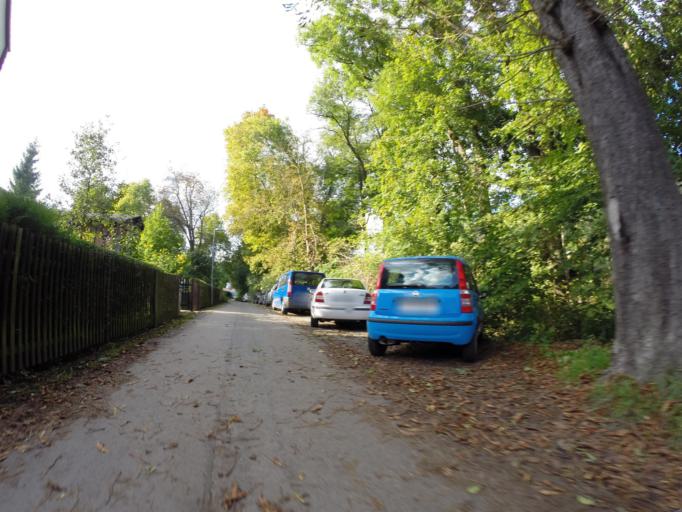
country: DE
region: Thuringia
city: Jena
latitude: 50.9342
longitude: 11.5618
